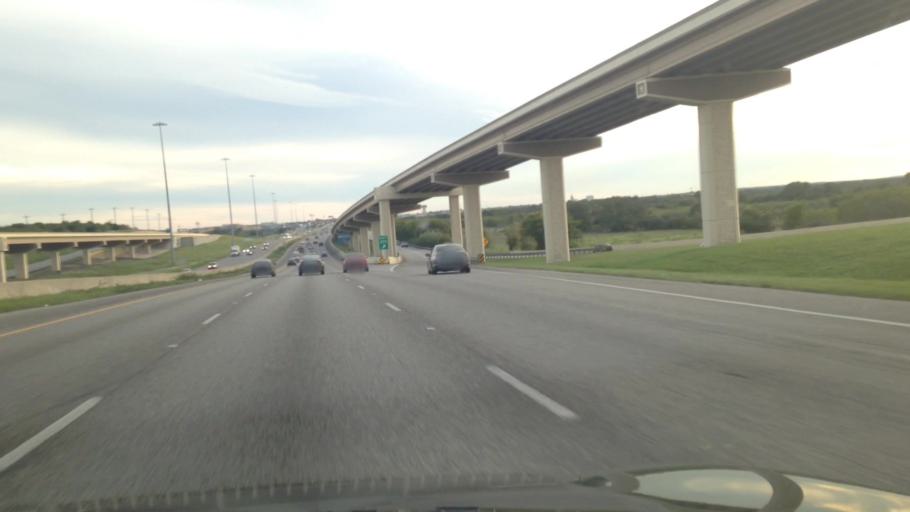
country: US
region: Texas
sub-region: Travis County
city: Onion Creek
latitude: 30.1099
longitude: -97.8086
